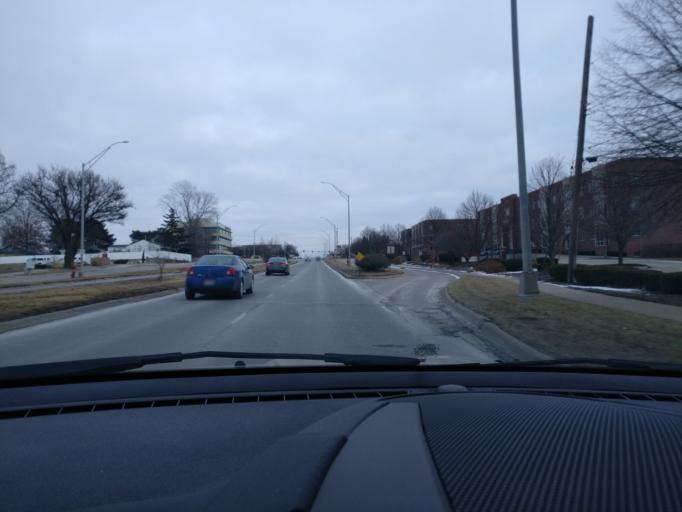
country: US
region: Nebraska
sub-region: Lancaster County
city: Lincoln
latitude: 40.8134
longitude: -96.6113
